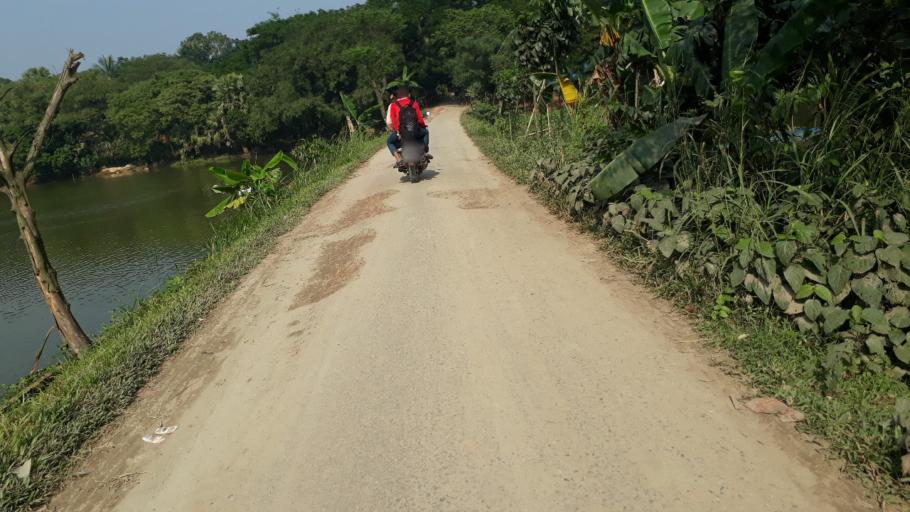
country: BD
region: Dhaka
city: Tungi
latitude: 23.8744
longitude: 90.2594
